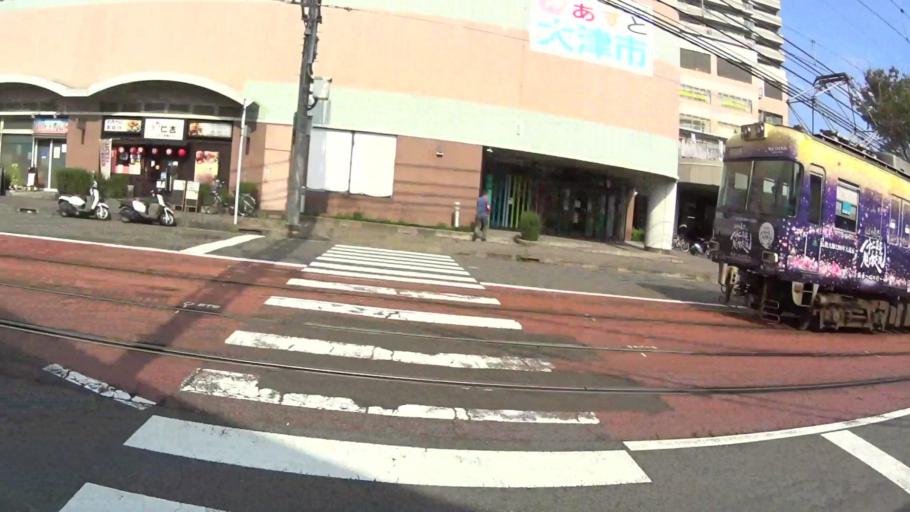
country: JP
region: Osaka
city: Izumiotsu
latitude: 34.5247
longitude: 135.3572
